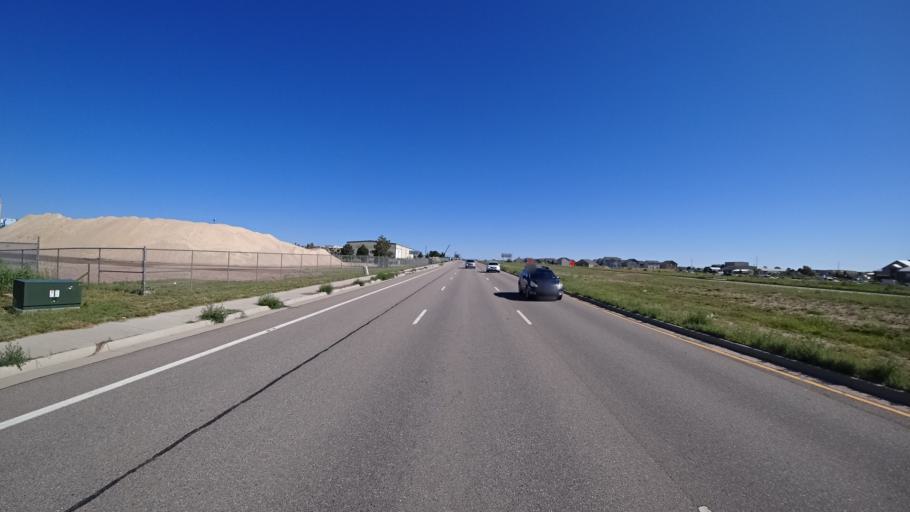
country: US
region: Colorado
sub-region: El Paso County
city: Cimarron Hills
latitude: 38.8718
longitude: -104.6829
